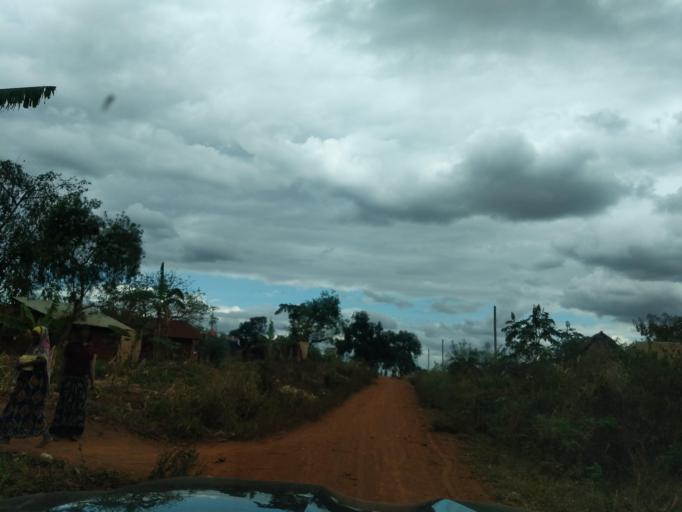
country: TZ
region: Pwani
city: Mvomero
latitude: -5.9417
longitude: 38.4230
